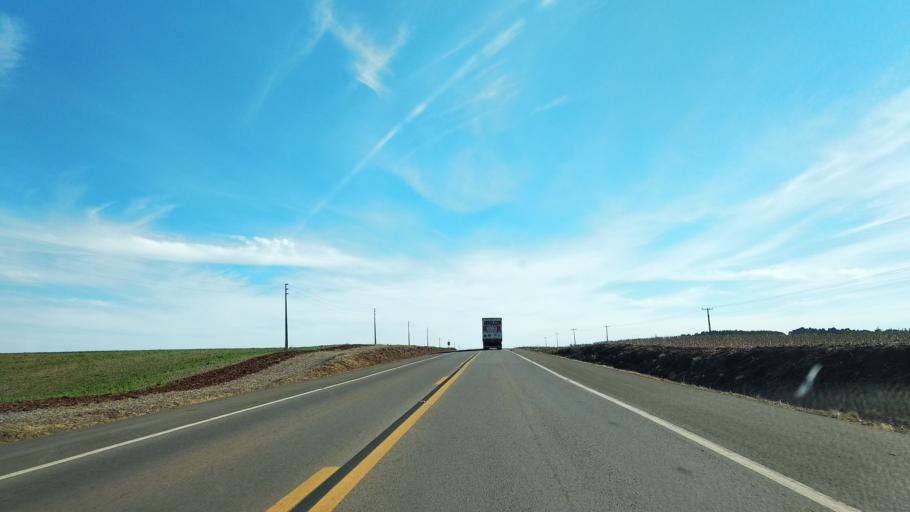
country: BR
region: Santa Catarina
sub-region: Campos Novos
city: Campos Novos
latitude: -27.4883
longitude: -51.3238
